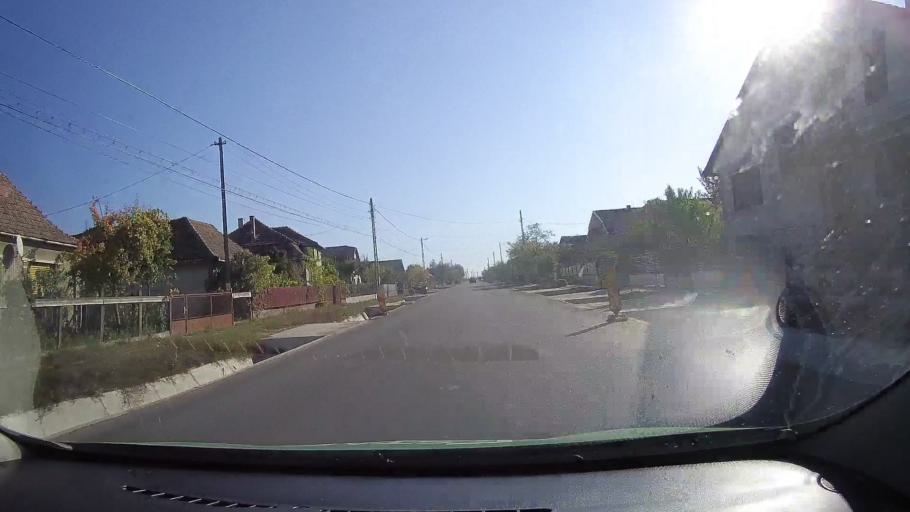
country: RO
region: Satu Mare
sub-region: Comuna Santau
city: Santau
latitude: 47.5098
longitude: 22.5138
